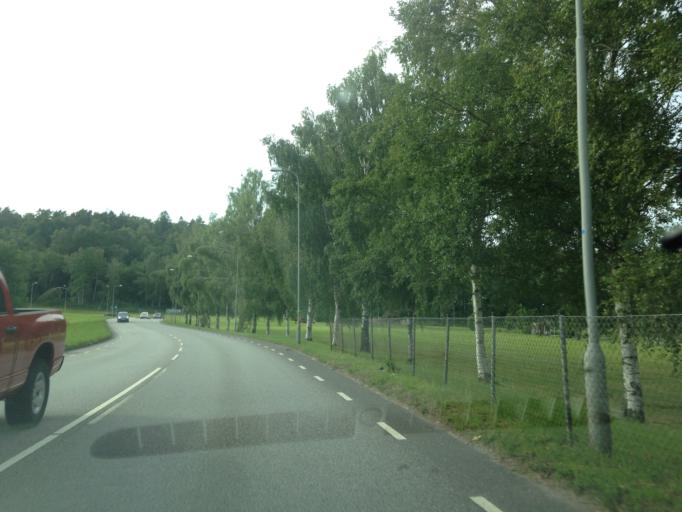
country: SE
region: Vaestra Goetaland
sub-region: Goteborg
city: Goeteborg
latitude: 57.7546
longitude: 11.9806
